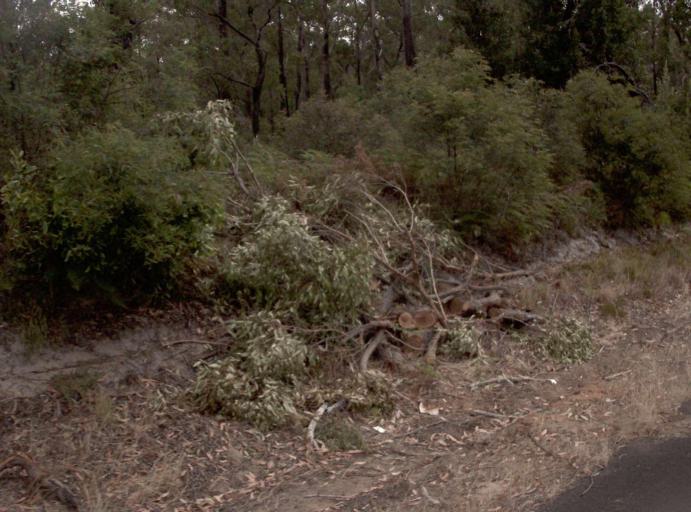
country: AU
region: Victoria
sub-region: Wellington
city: Sale
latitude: -38.4000
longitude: 146.9698
